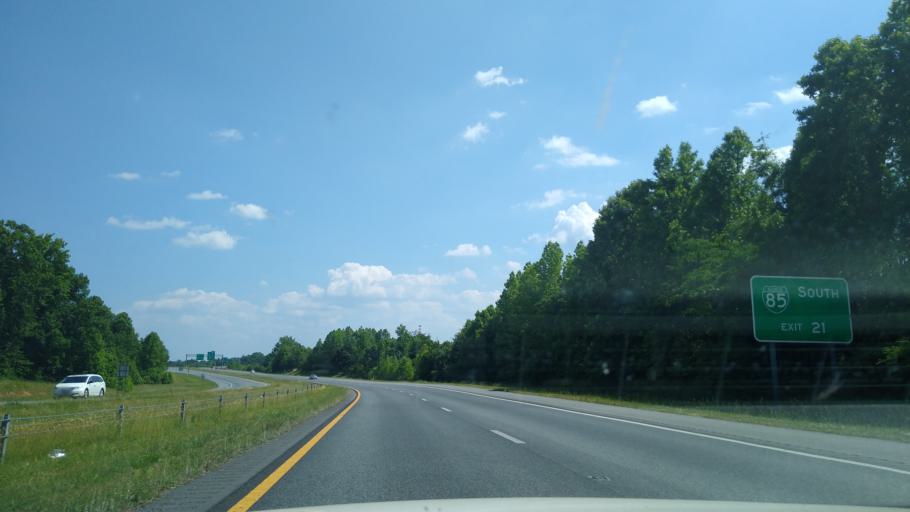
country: US
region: North Carolina
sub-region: Guilford County
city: McLeansville
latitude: 36.0687
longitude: -79.6909
